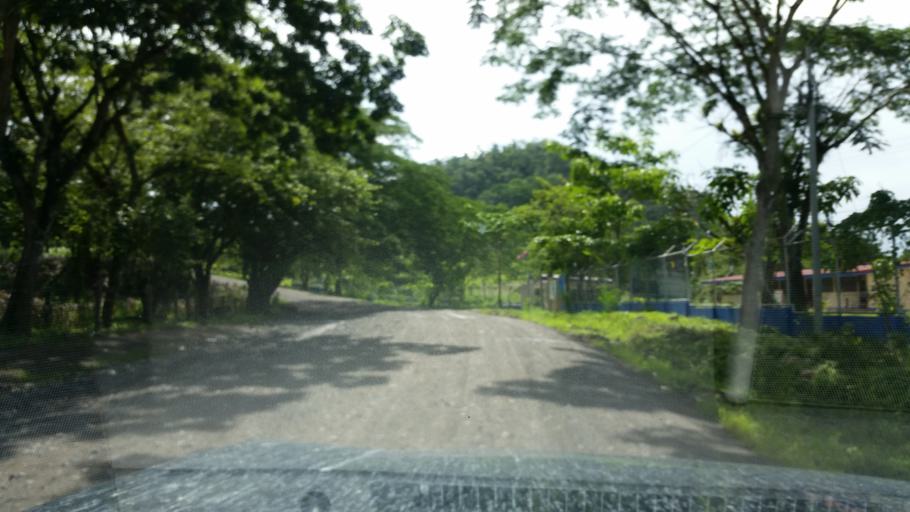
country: NI
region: Atlantico Norte (RAAN)
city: Siuna
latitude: 13.7185
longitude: -84.7641
